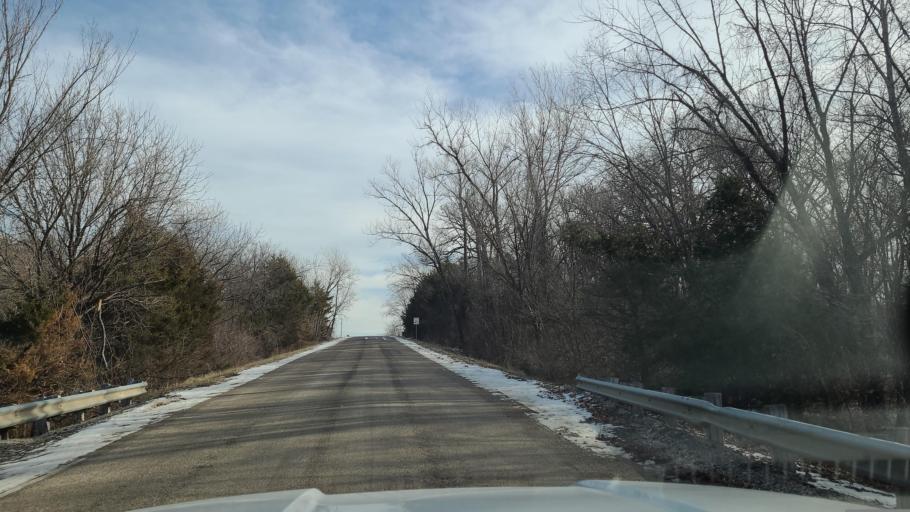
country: US
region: Kansas
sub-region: Douglas County
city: Lawrence
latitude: 38.8990
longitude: -95.1962
